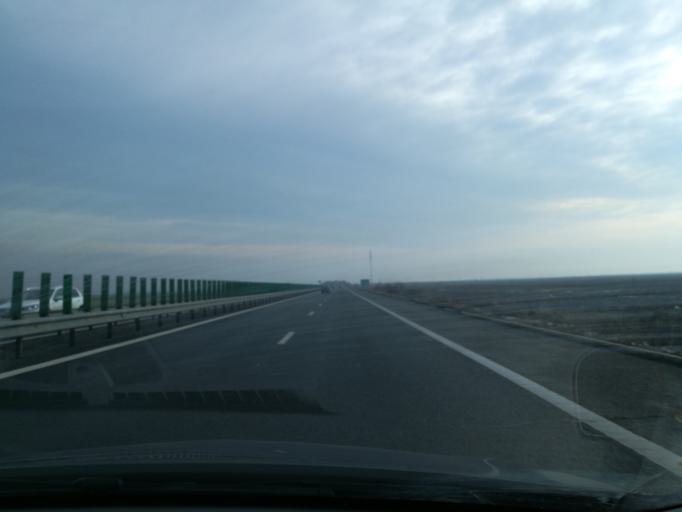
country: RO
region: Calarasi
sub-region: Comuna Dragalina
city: Dragalina
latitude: 44.4159
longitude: 27.3190
